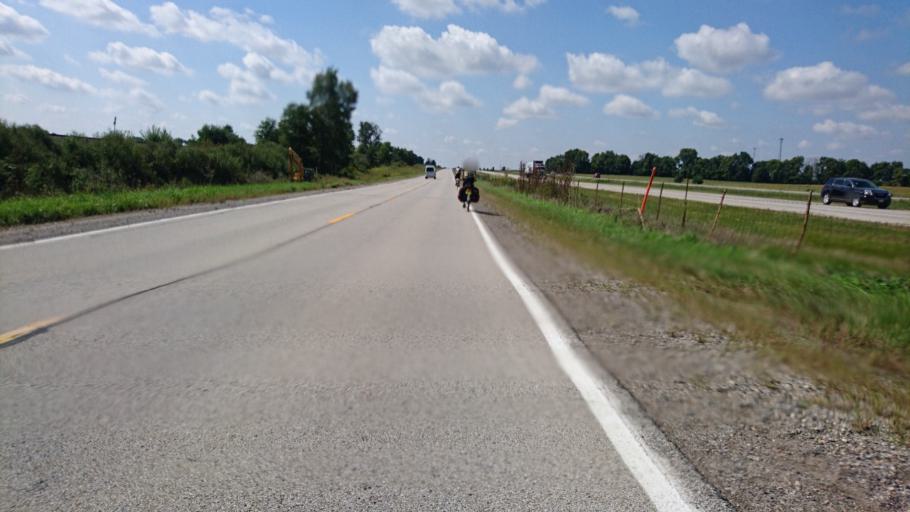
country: US
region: Illinois
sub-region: McLean County
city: Lexington
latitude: 40.6000
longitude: -88.8456
